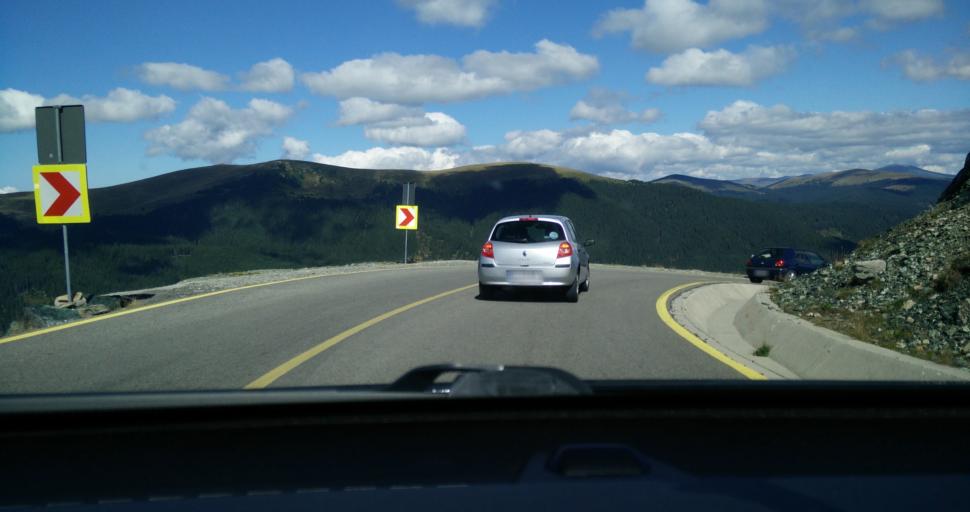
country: RO
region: Gorj
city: Novaci-Straini
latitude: 45.3812
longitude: 23.6419
